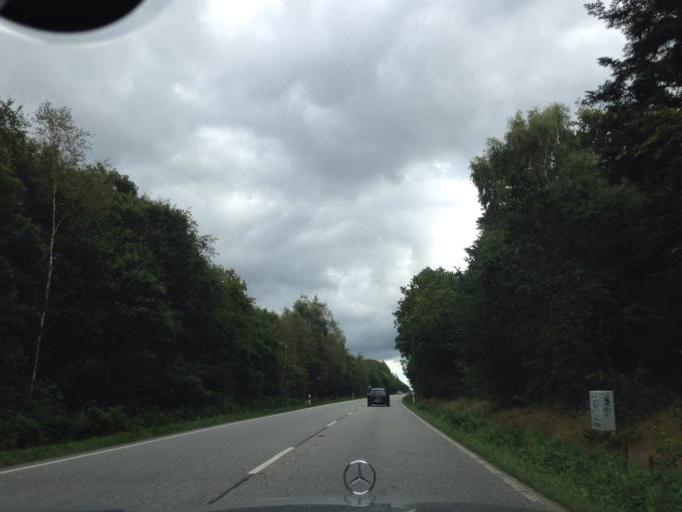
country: DE
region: Schleswig-Holstein
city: Leck
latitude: 54.7514
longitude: 9.0101
